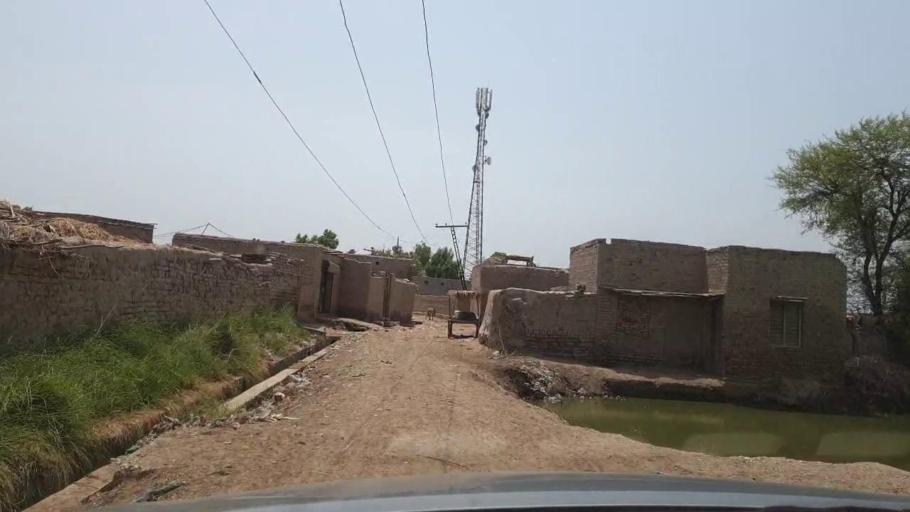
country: PK
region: Sindh
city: Madeji
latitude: 27.7621
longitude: 68.3833
